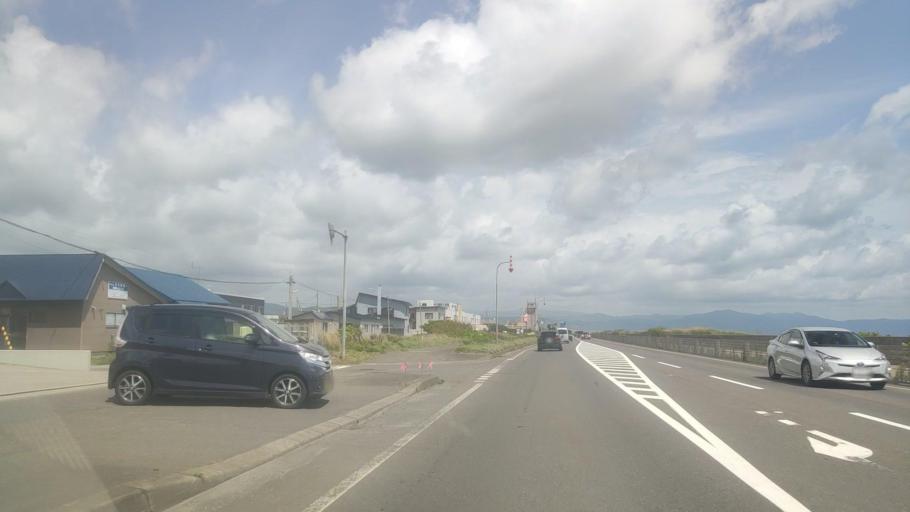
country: JP
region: Hokkaido
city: Niseko Town
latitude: 42.5081
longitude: 140.3757
